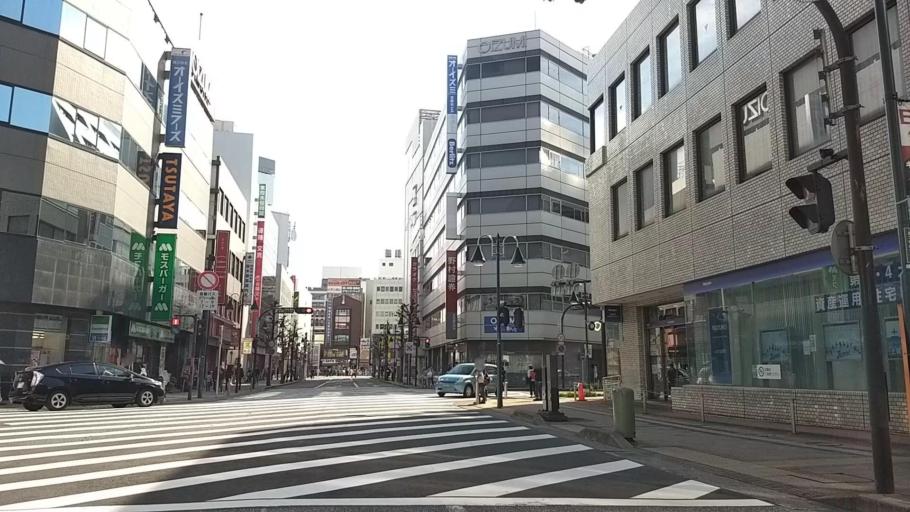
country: JP
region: Kanagawa
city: Atsugi
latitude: 35.4412
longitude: 139.3630
